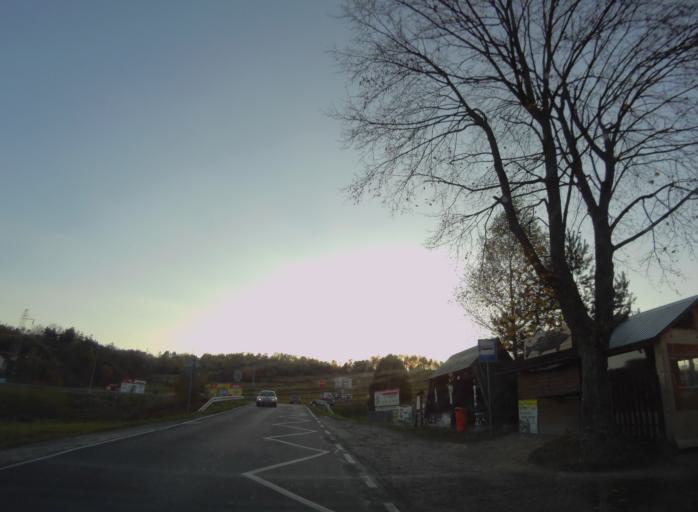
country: PL
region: Subcarpathian Voivodeship
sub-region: Powiat leski
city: Polanczyk
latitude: 49.3770
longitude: 22.4180
